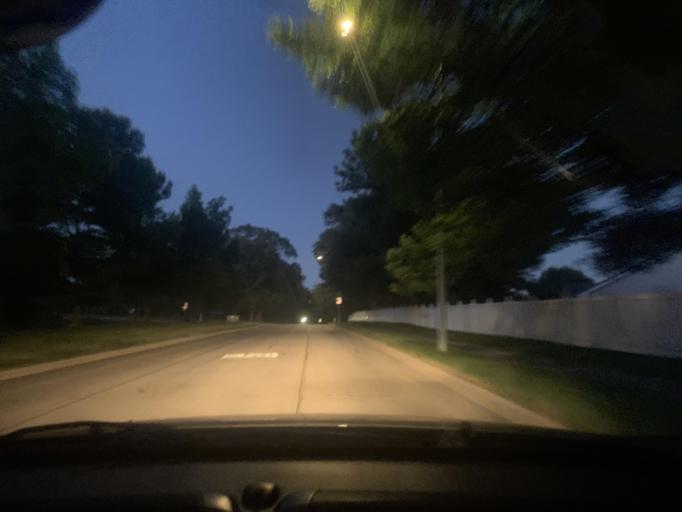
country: US
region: Nebraska
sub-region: Sarpy County
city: La Vista
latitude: 41.1780
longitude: -96.0571
